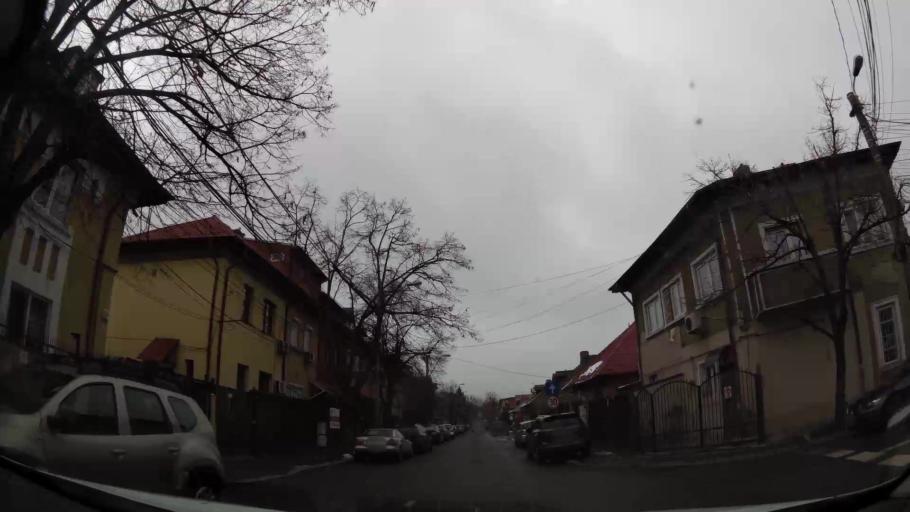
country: RO
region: Bucuresti
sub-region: Municipiul Bucuresti
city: Bucuresti
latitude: 44.4615
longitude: 26.0619
